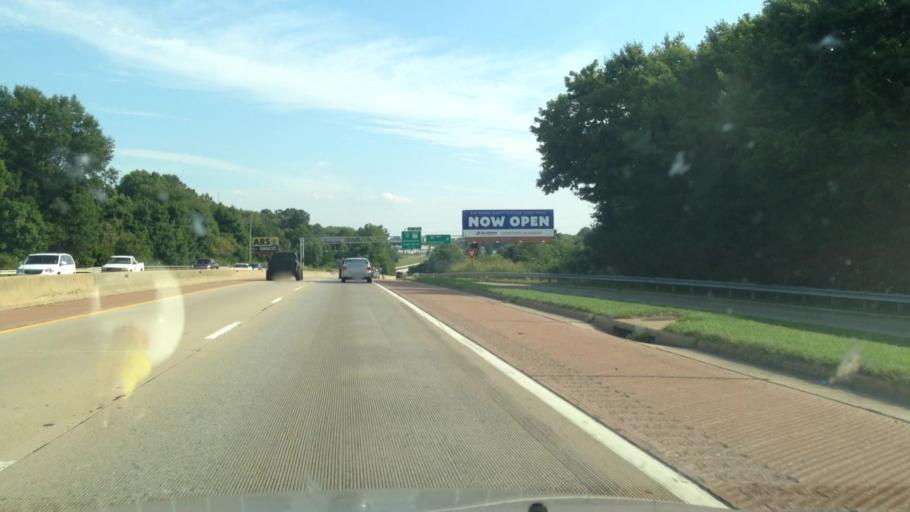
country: US
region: North Carolina
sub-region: Forsyth County
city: Winston-Salem
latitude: 36.0676
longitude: -80.2290
